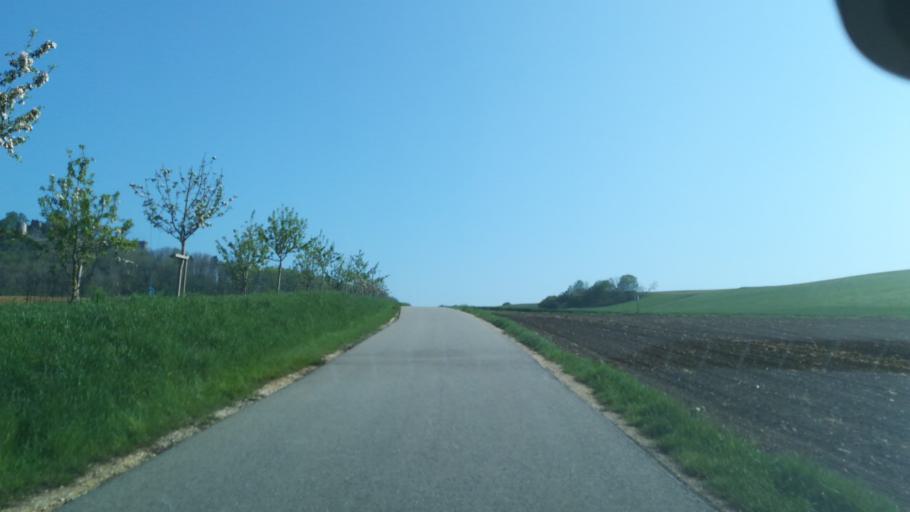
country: DE
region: Baden-Wuerttemberg
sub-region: Freiburg Region
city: Muhlhausen-Ehingen
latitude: 47.7998
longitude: 8.7957
